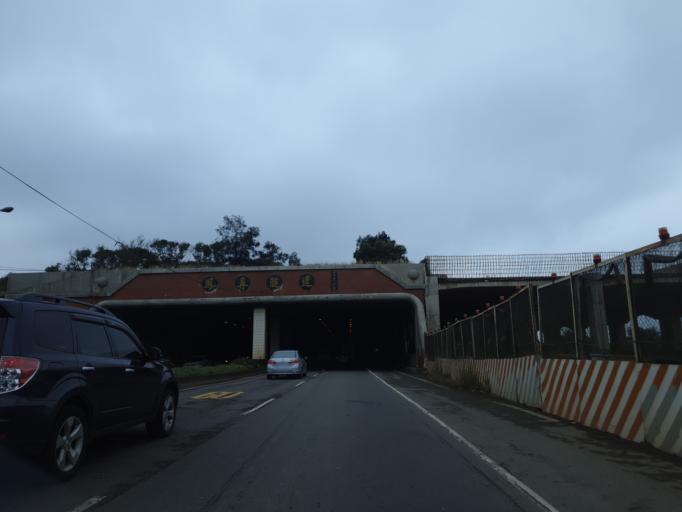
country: TW
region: Taiwan
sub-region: Hsinchu
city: Zhubei
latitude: 24.8958
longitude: 120.9645
